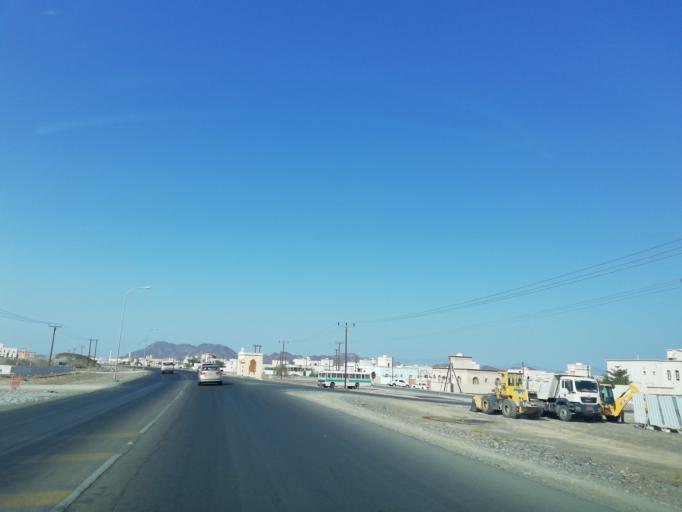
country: OM
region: Ash Sharqiyah
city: Ibra'
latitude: 22.7921
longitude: 58.1485
